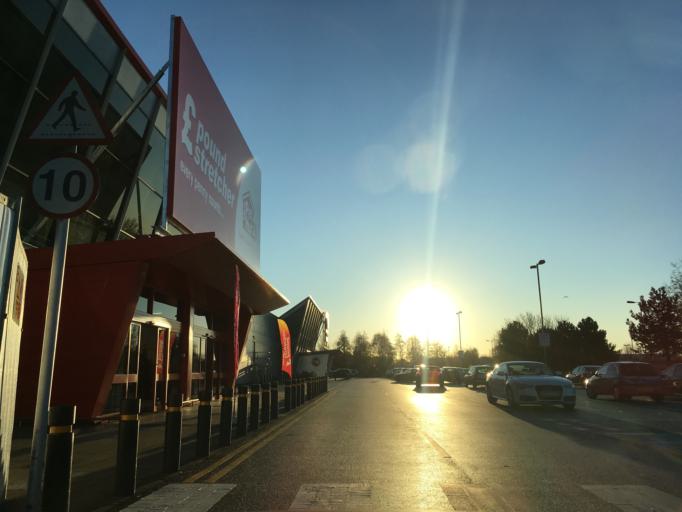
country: GB
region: England
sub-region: South Gloucestershire
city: Stoke Gifford
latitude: 51.5075
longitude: -2.5511
